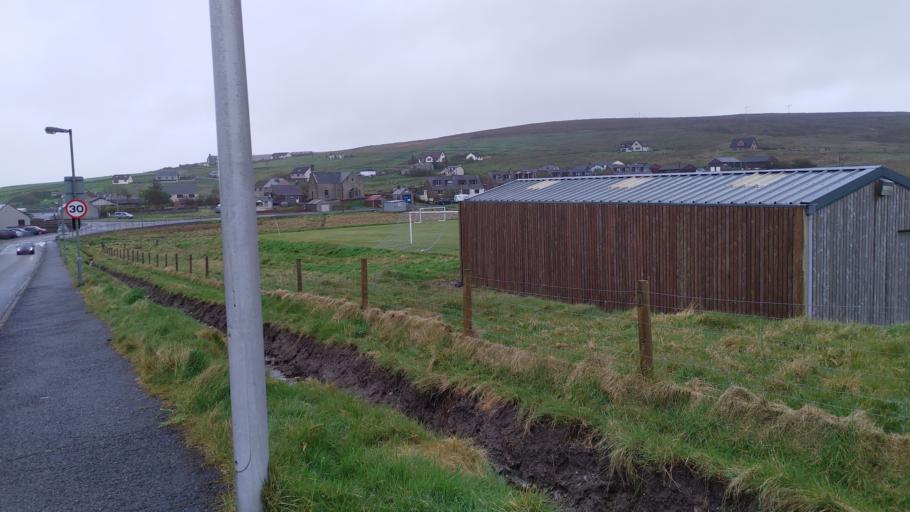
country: GB
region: Scotland
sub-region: Shetland Islands
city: Shetland
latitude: 60.5980
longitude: -1.0647
